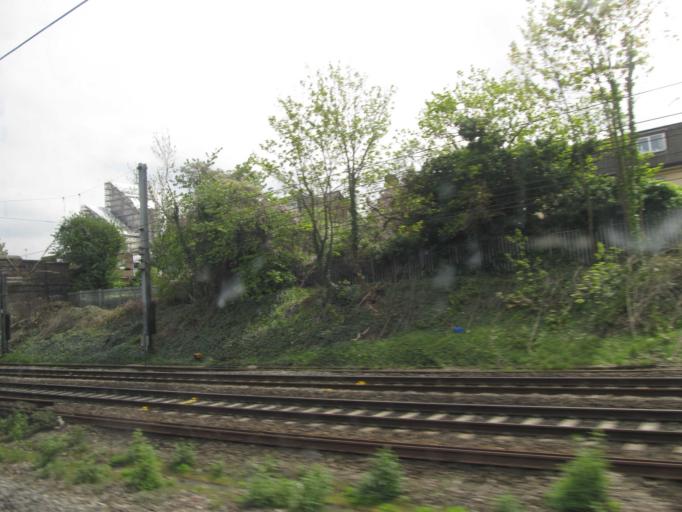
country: GB
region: England
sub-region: Greater London
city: Ealing
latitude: 51.5138
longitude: -0.3154
